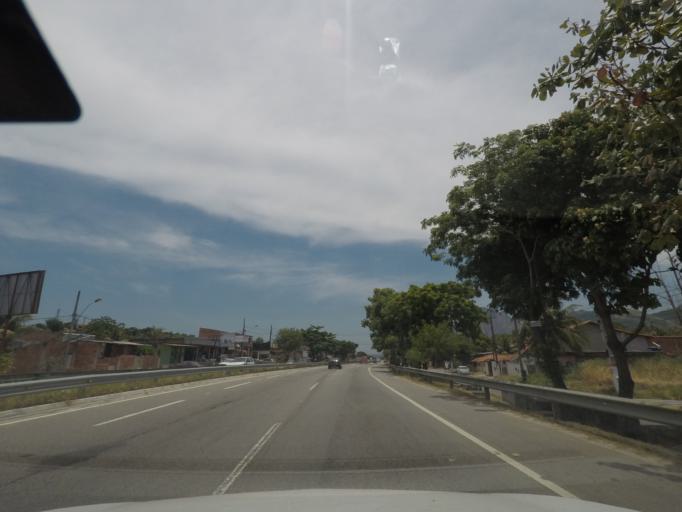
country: BR
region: Rio de Janeiro
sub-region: Marica
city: Marica
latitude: -22.9308
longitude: -42.8764
